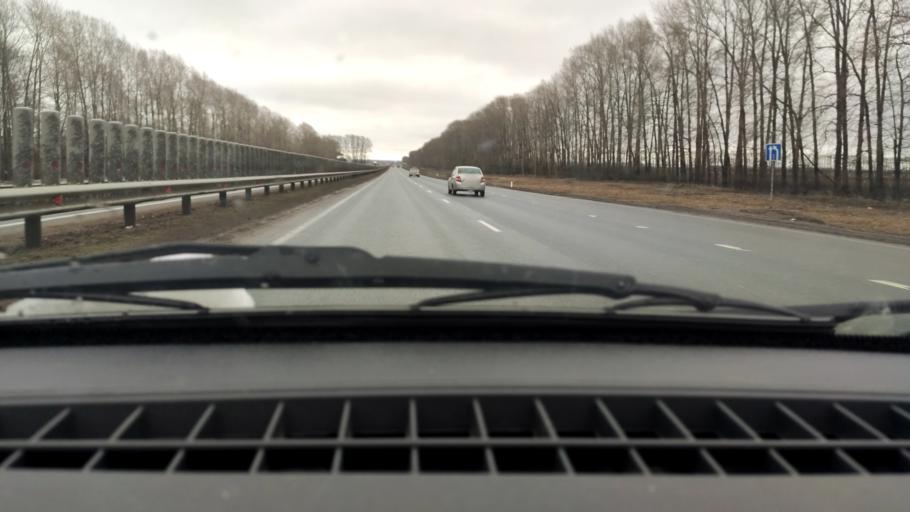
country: RU
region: Bashkortostan
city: Asanovo
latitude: 55.0218
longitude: 55.4724
